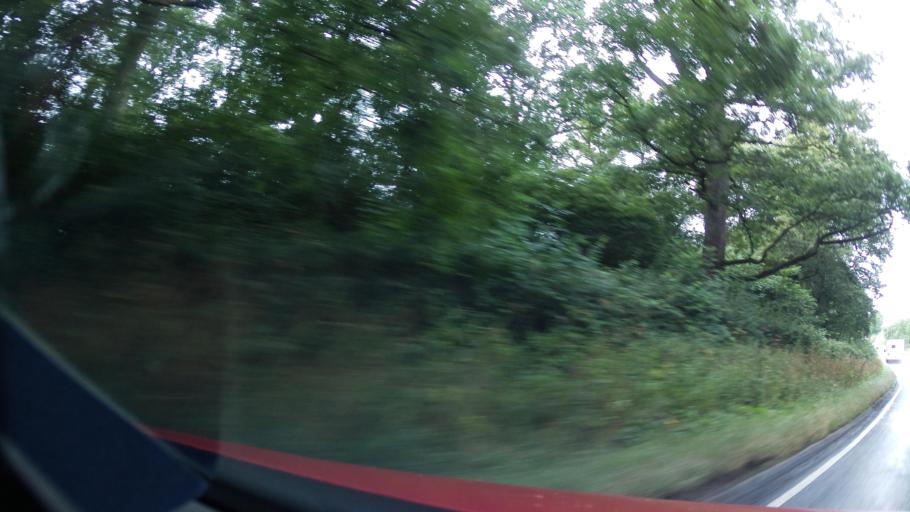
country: GB
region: England
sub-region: Worcestershire
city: Fernhill Heath
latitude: 52.1901
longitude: -2.1460
